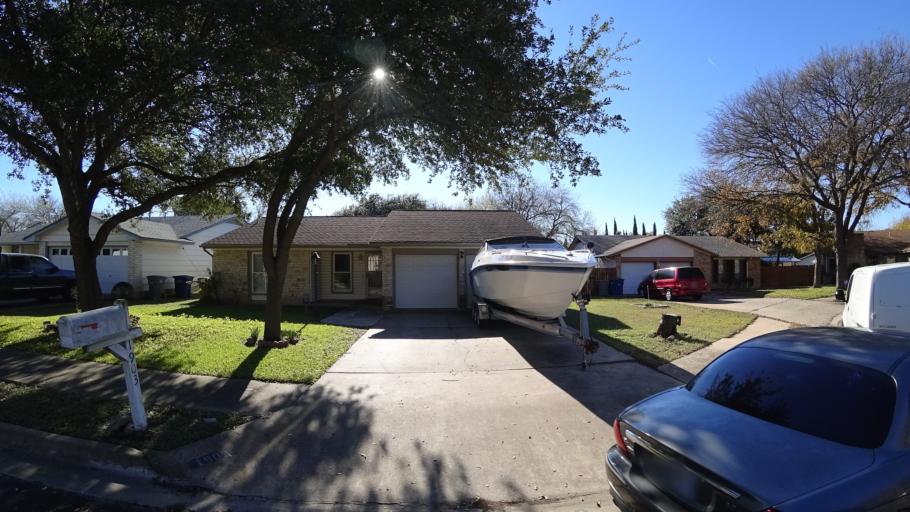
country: US
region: Texas
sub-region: Travis County
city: Wells Branch
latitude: 30.4184
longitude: -97.6910
